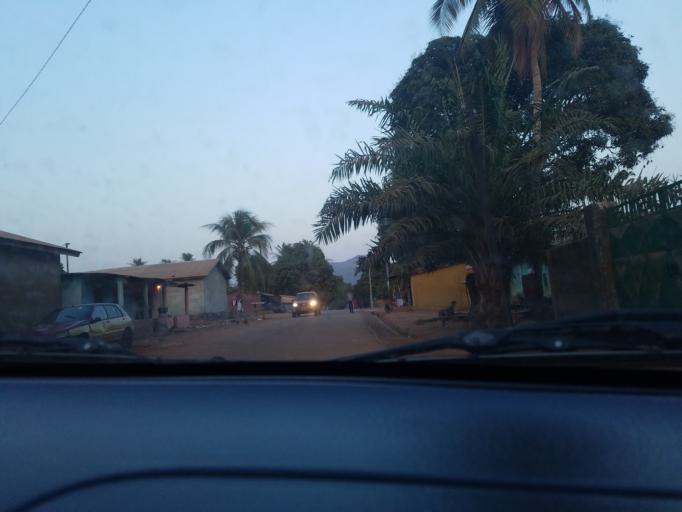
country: GN
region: Kindia
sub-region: Prefecture de Dubreka
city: Dubreka
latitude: 9.7877
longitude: -13.5207
